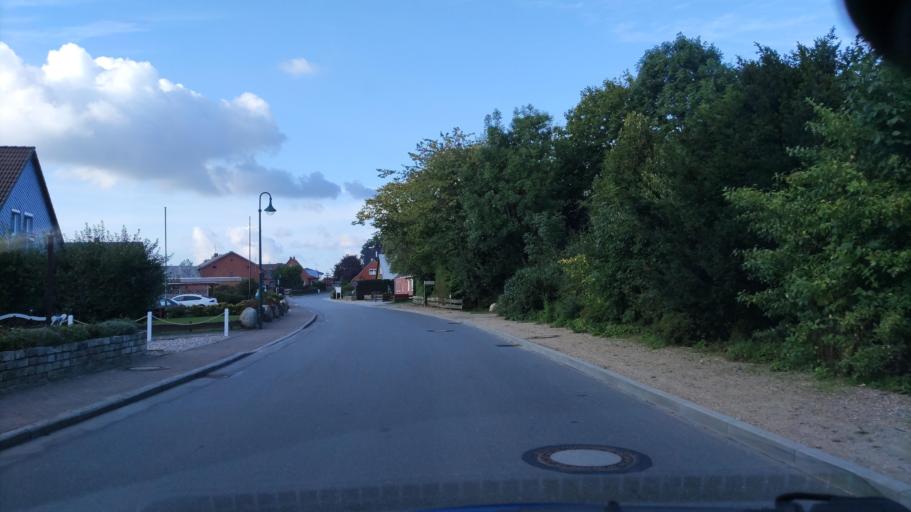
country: DE
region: Schleswig-Holstein
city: Glasau
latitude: 54.0551
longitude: 10.5315
